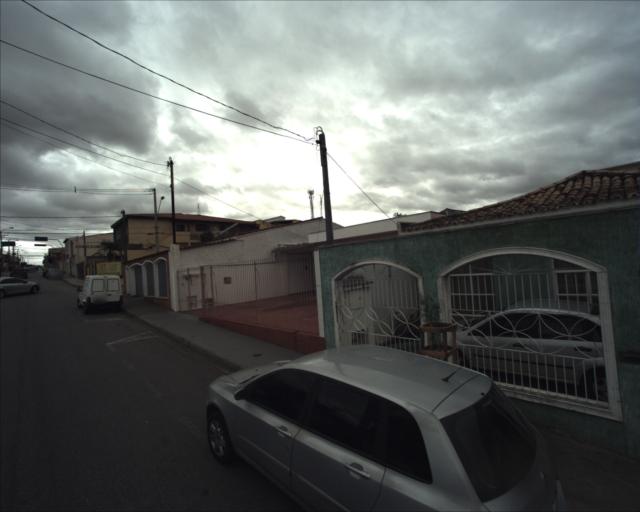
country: BR
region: Sao Paulo
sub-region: Sorocaba
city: Sorocaba
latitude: -23.4766
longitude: -47.4629
